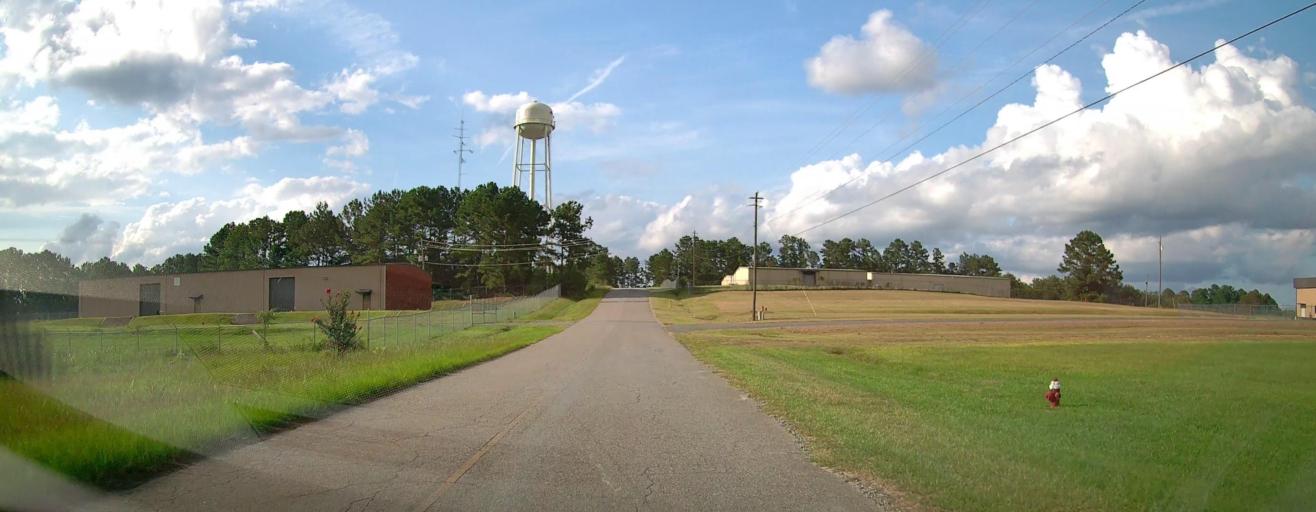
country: US
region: Georgia
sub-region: Crawford County
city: Roberta
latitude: 32.7195
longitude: -84.0207
